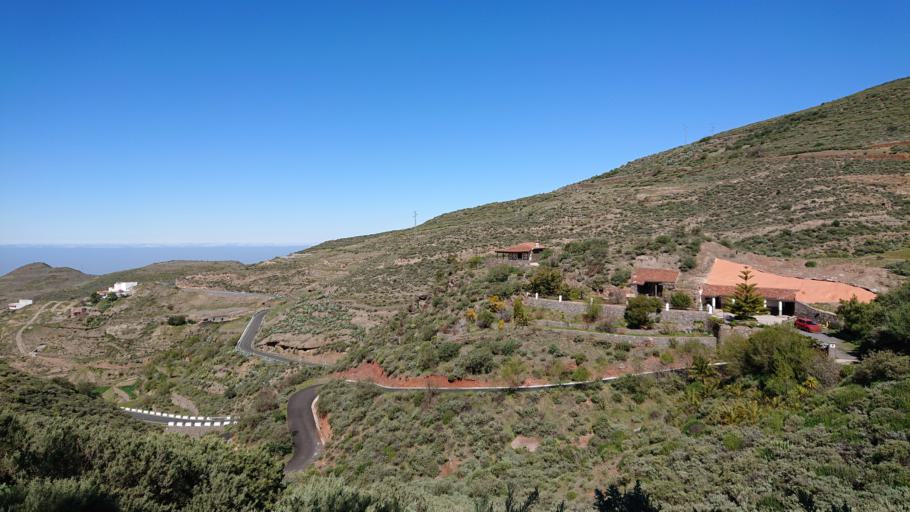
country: ES
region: Canary Islands
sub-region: Provincia de Las Palmas
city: Artenara
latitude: 28.0194
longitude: -15.6427
